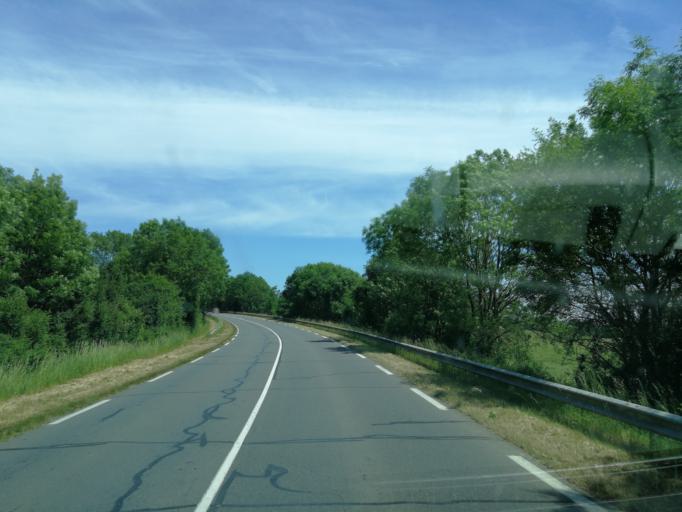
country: FR
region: Pays de la Loire
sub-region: Departement de la Vendee
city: La Chataigneraie
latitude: 46.6387
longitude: -0.7451
